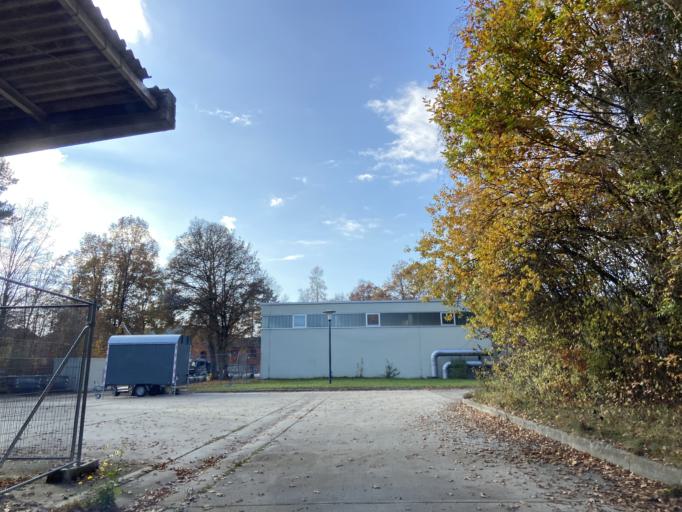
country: DE
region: Baden-Wuerttemberg
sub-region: Tuebingen Region
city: Sigmaringen
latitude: 48.0932
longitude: 9.2466
